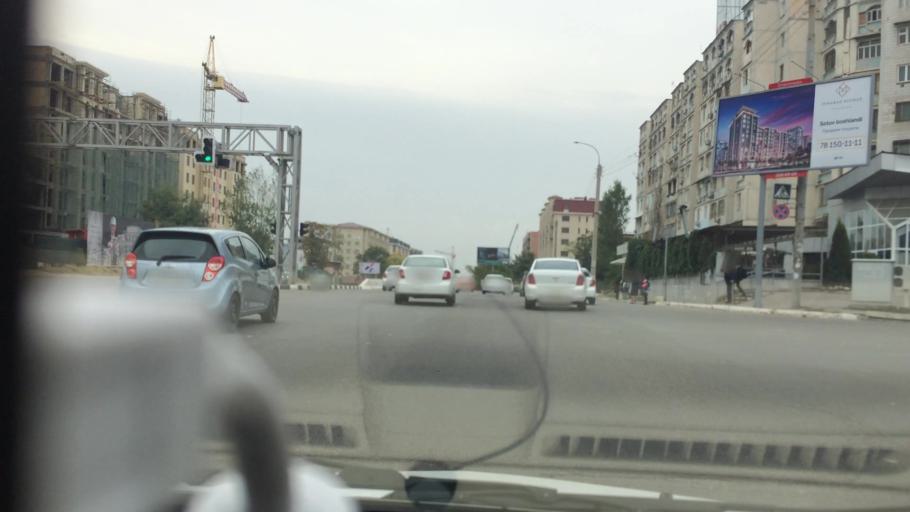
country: UZ
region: Toshkent
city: Salor
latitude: 41.3129
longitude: 69.3310
